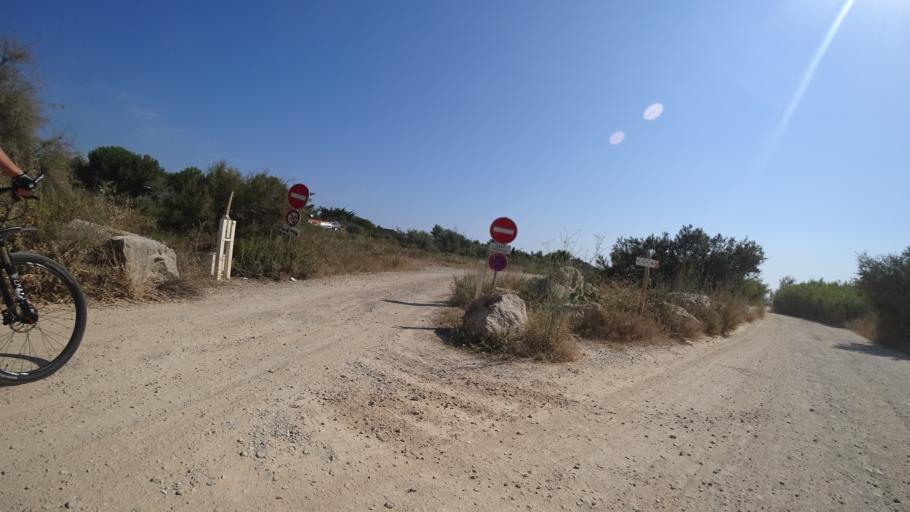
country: FR
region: Languedoc-Roussillon
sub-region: Departement des Pyrenees-Orientales
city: Le Barcares
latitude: 42.7579
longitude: 3.0335
